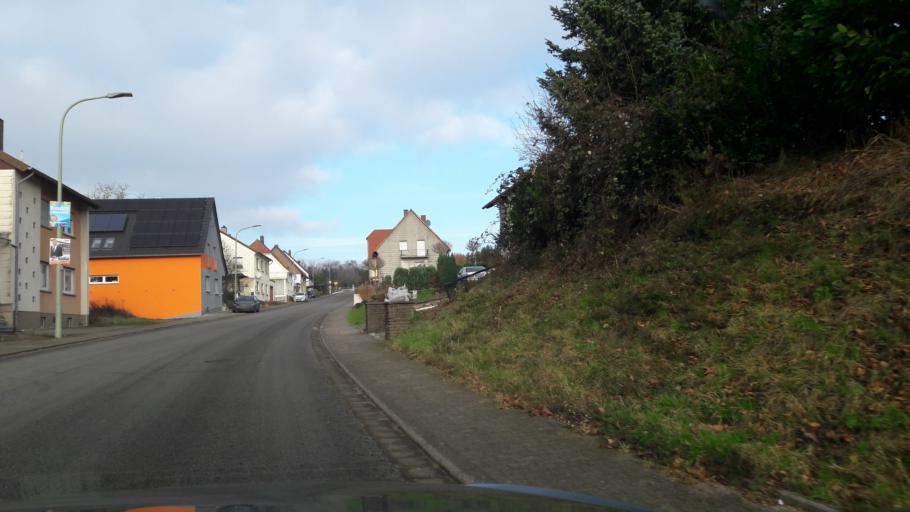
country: DE
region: Rheinland-Pfalz
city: Brucken
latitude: 49.4350
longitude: 7.3665
